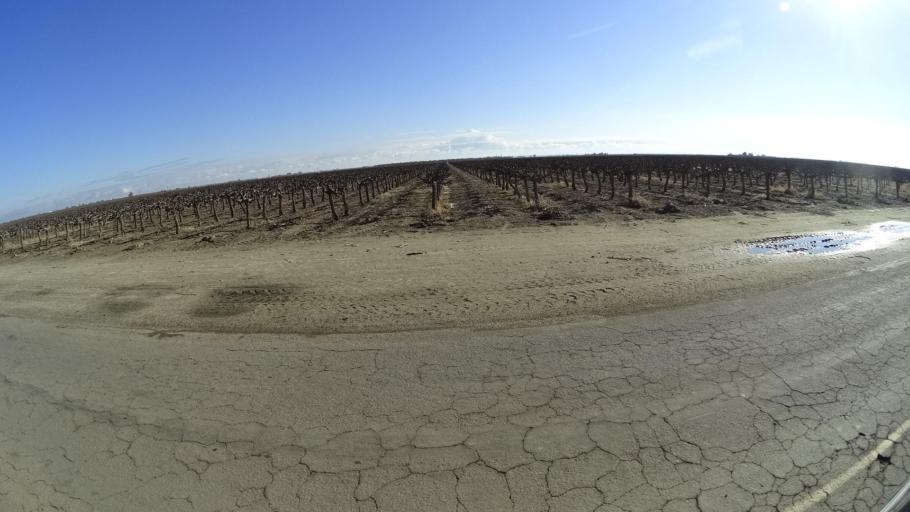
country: US
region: California
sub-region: Kern County
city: Delano
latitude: 35.7232
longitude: -119.2763
